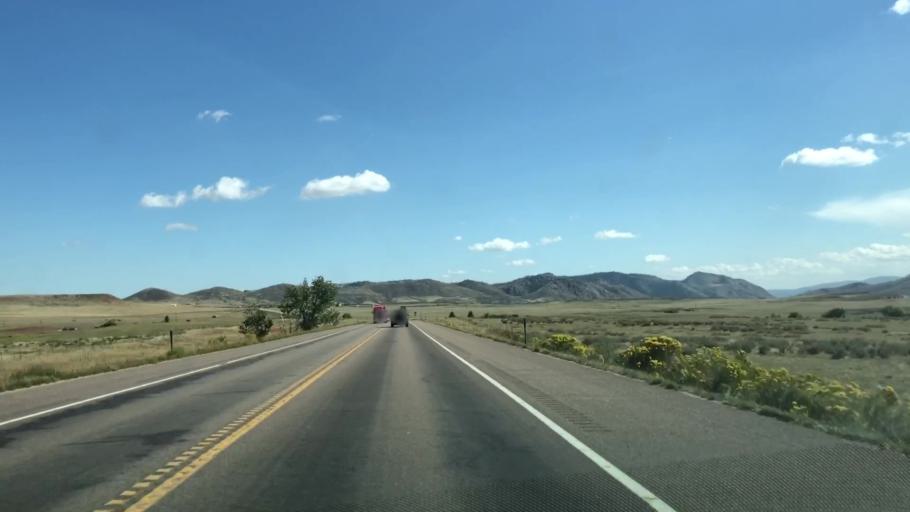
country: US
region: Colorado
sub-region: Larimer County
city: Laporte
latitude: 40.8122
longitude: -105.2406
